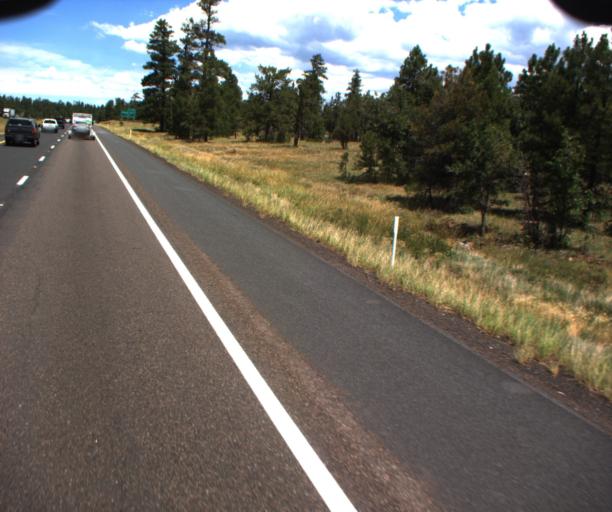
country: US
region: Arizona
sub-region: Coconino County
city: Sedona
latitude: 34.9256
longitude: -111.6462
